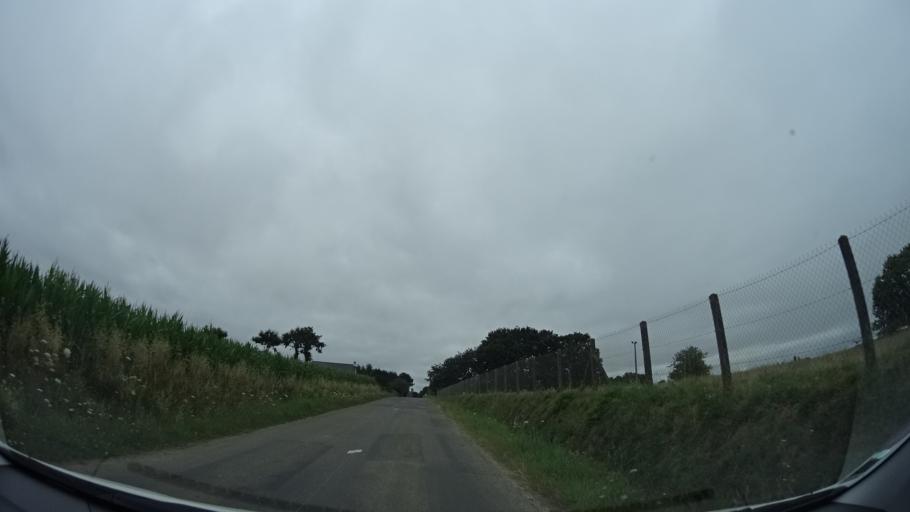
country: FR
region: Brittany
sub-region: Departement des Cotes-d'Armor
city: Evran
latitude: 48.3322
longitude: -1.9330
